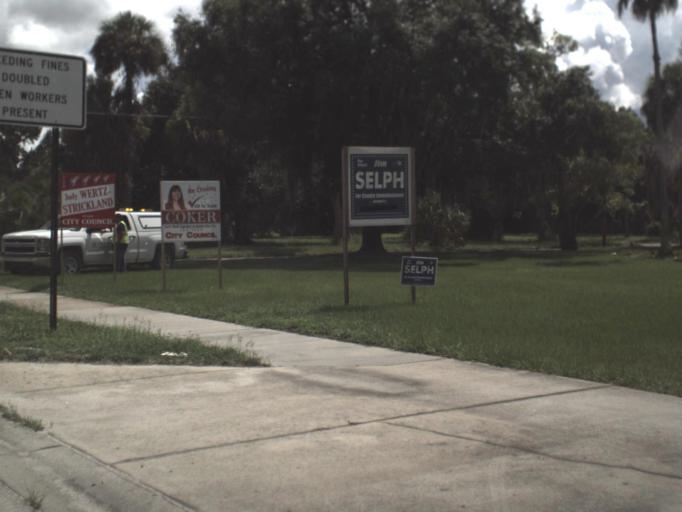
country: US
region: Florida
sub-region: DeSoto County
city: Arcadia
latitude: 27.2137
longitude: -81.8587
